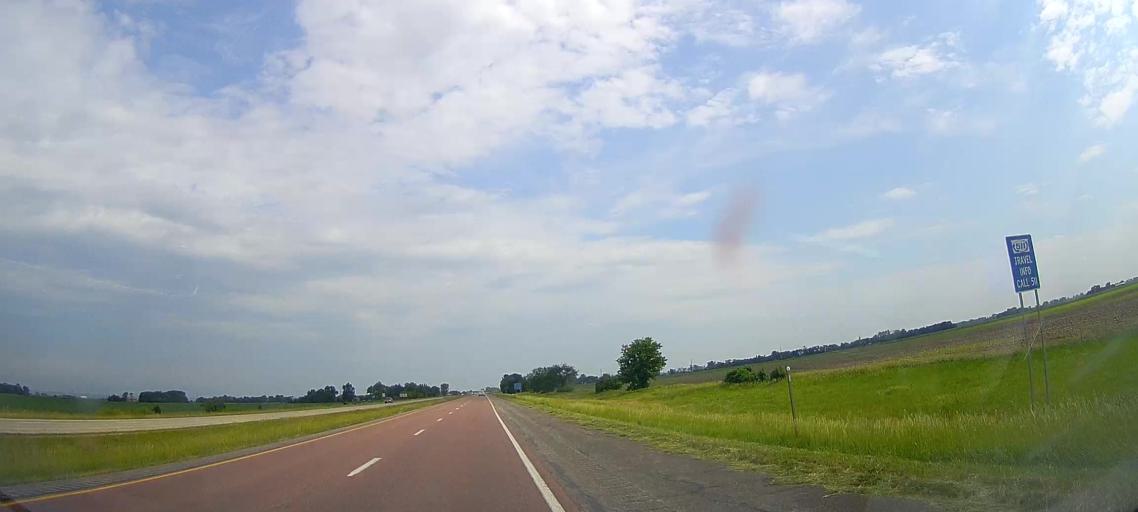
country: US
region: Iowa
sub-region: Monona County
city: Onawa
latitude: 42.0033
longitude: -96.1156
